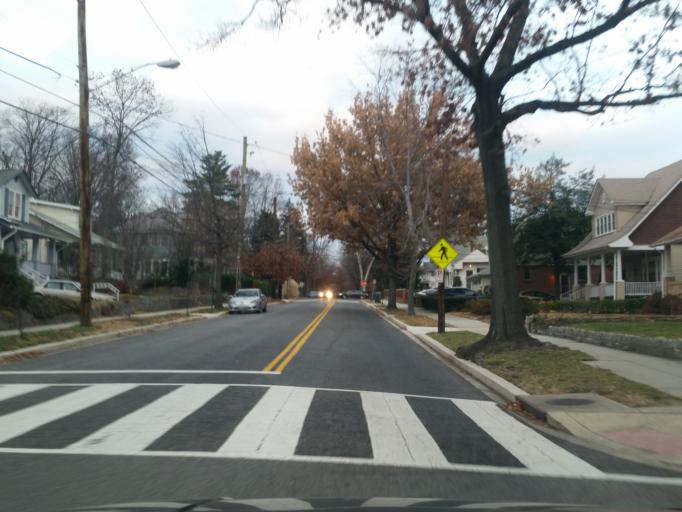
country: US
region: Maryland
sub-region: Montgomery County
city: Takoma Park
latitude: 38.9713
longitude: -77.0199
